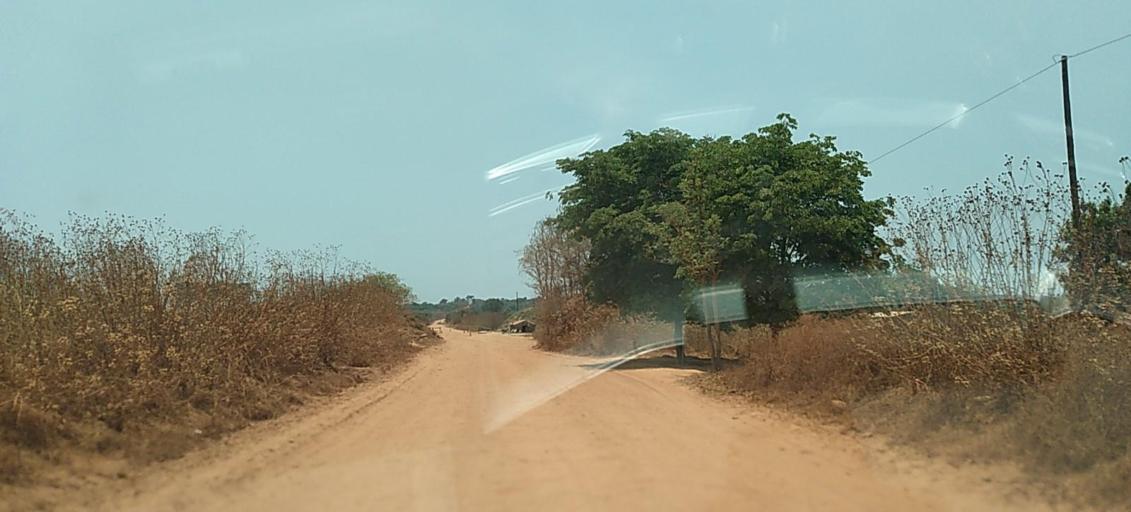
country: CD
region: Katanga
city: Kipushi
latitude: -11.7794
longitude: 27.1911
